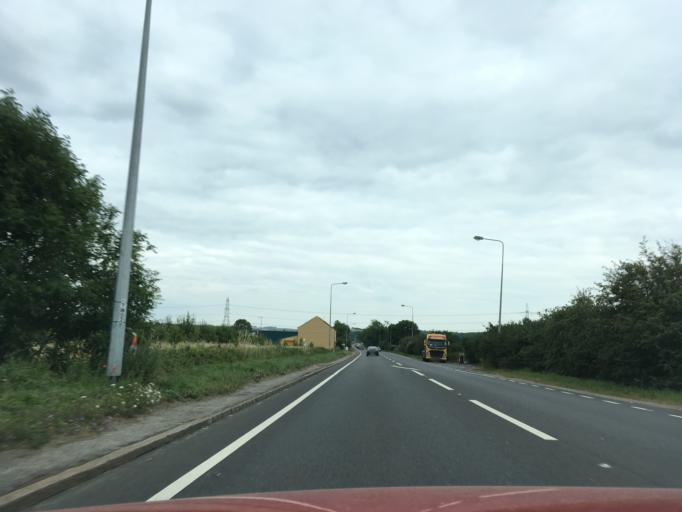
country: GB
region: England
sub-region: Central Bedfordshire
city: Hockliffe
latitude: 51.9150
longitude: -0.5626
